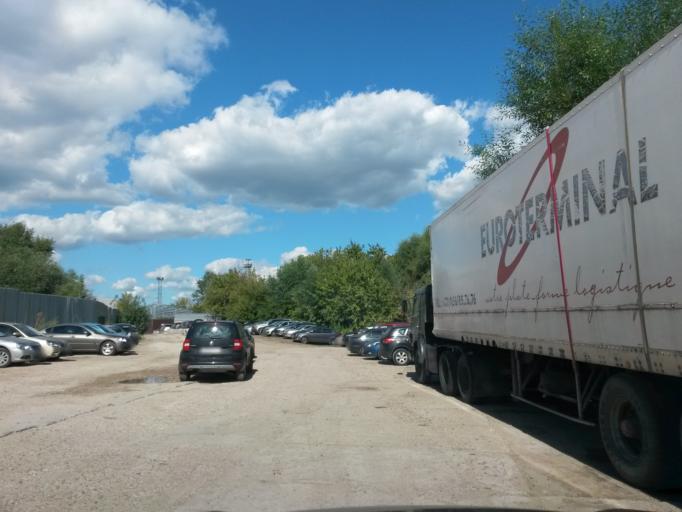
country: RU
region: Moskovskaya
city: Kozhukhovo
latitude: 55.7020
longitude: 37.6987
